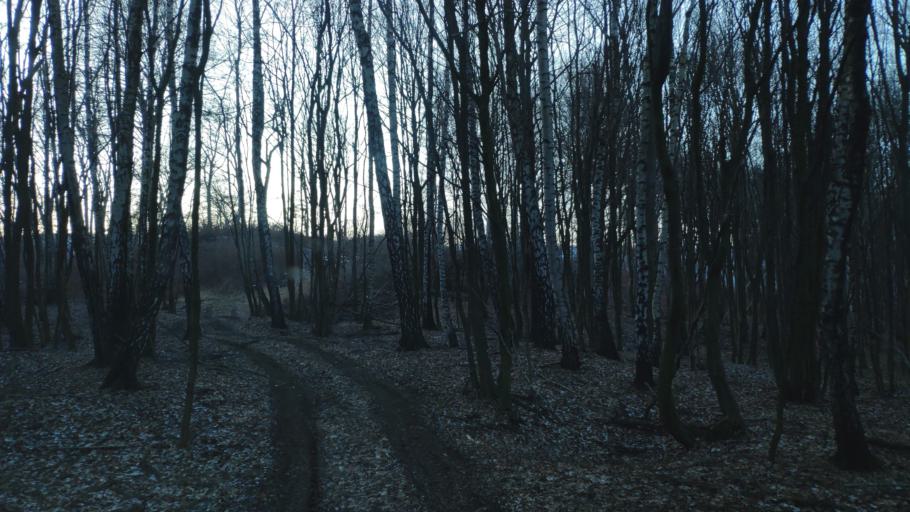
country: SK
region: Kosicky
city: Kosice
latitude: 48.8518
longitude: 21.2344
